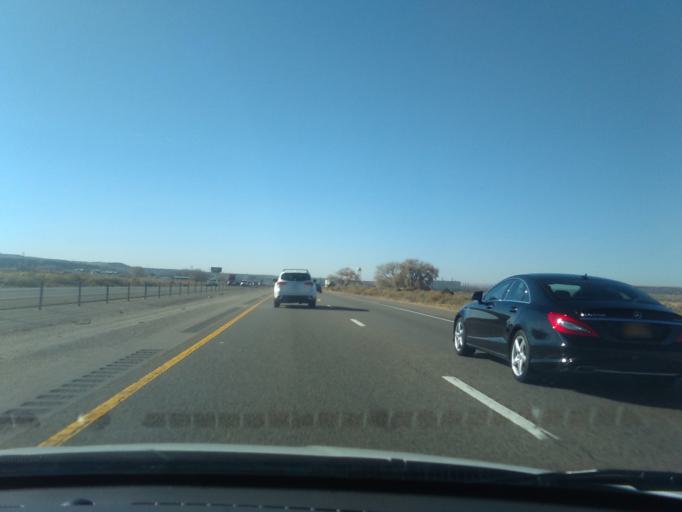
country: US
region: New Mexico
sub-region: Sandoval County
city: San Felipe Pueblo
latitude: 35.3906
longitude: -106.4543
